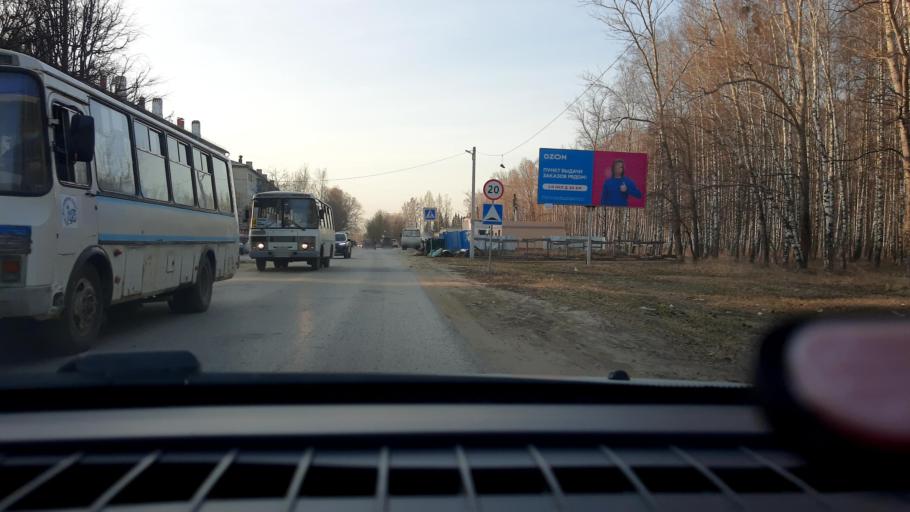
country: RU
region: Nizjnij Novgorod
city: Bogorodsk
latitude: 56.0995
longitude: 43.4799
